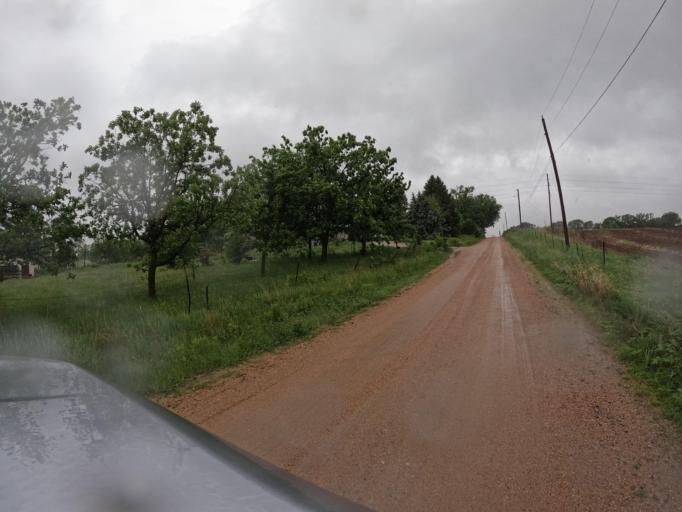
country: US
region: Nebraska
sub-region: Gage County
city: Wymore
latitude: 40.1275
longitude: -96.6537
